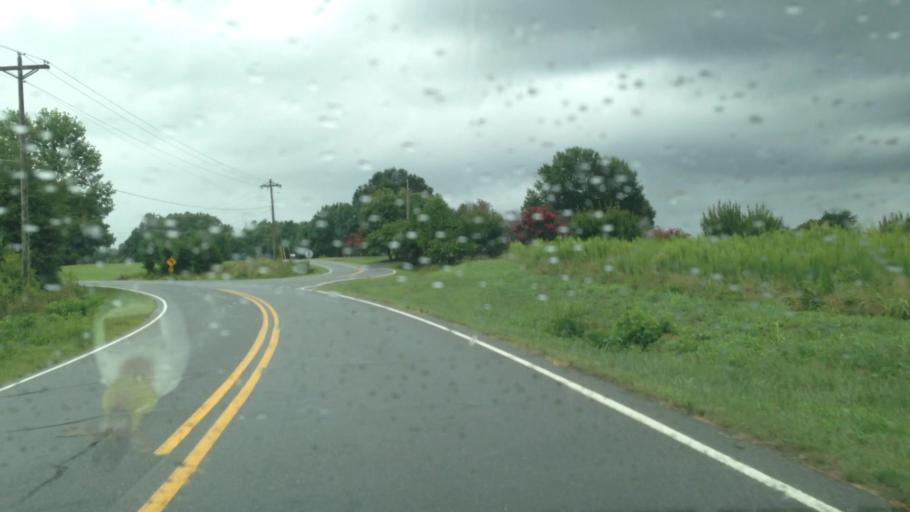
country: US
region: North Carolina
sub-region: Stokes County
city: Walnut Cove
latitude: 36.2638
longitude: -80.0986
